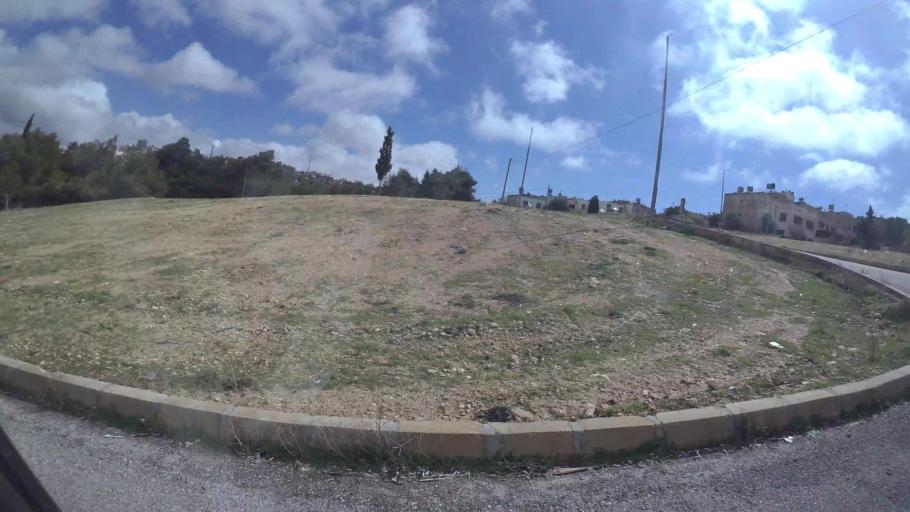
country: JO
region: Amman
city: Al Jubayhah
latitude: 32.0536
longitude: 35.8727
